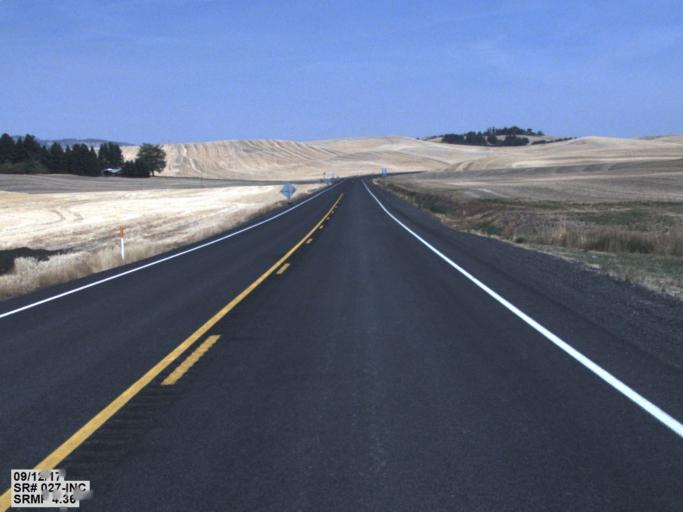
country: US
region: Washington
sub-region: Whitman County
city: Pullman
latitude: 46.7870
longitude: -117.1481
